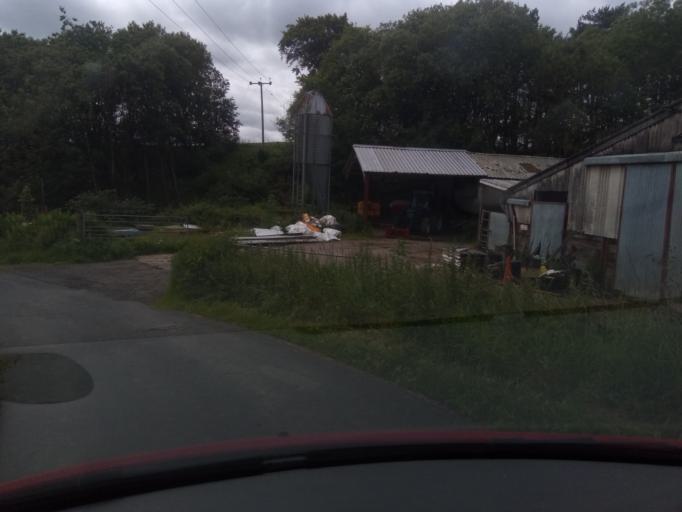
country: GB
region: Scotland
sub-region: The Scottish Borders
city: Hawick
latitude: 55.4318
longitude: -2.8213
